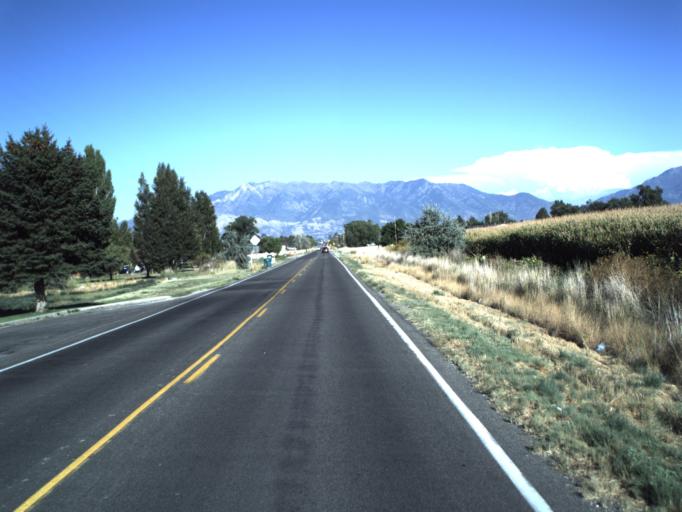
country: US
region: Utah
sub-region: Weber County
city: Hooper
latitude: 41.1907
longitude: -112.1196
